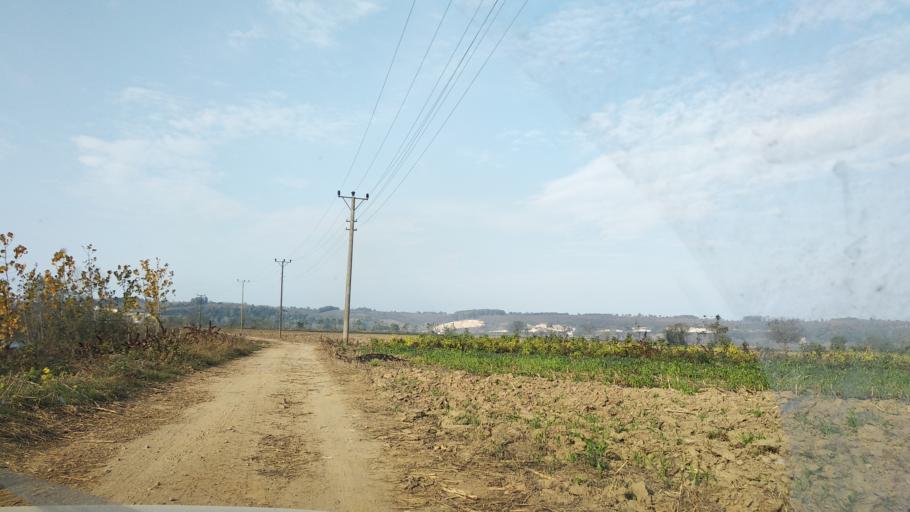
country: TR
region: Sakarya
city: Karasu
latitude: 41.0847
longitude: 30.6022
